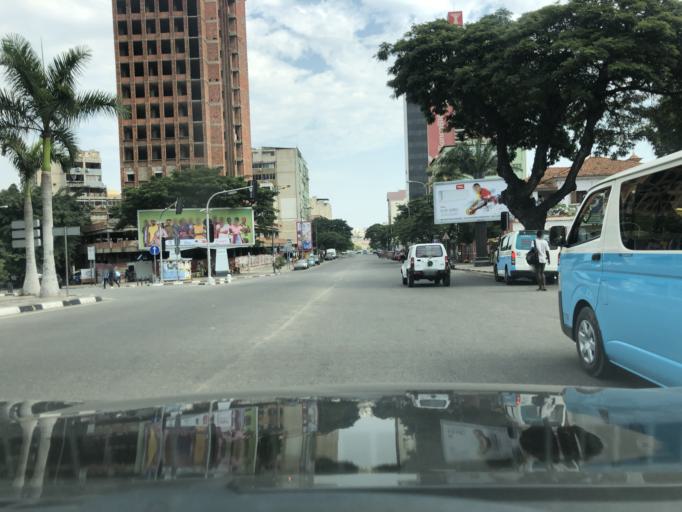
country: AO
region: Luanda
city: Luanda
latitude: -8.8229
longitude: 13.2291
